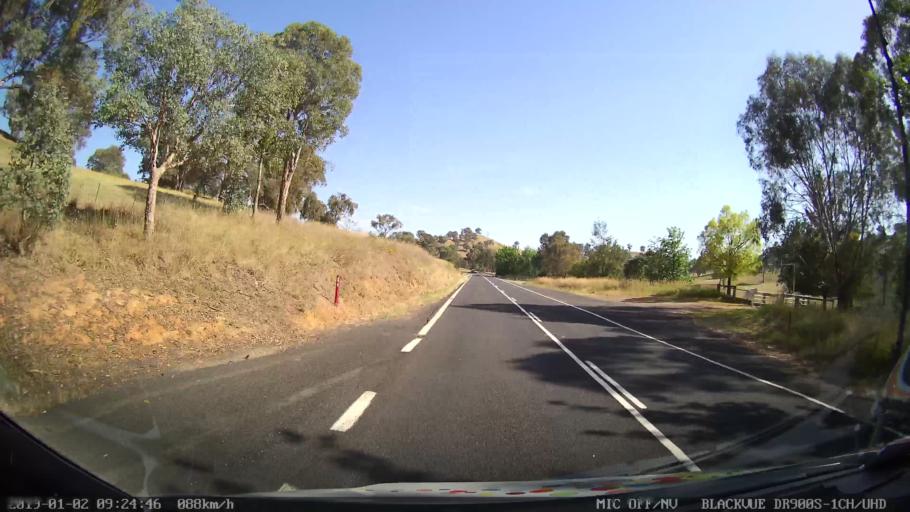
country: AU
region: New South Wales
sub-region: Tumut Shire
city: Tumut
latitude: -35.3726
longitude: 148.2918
